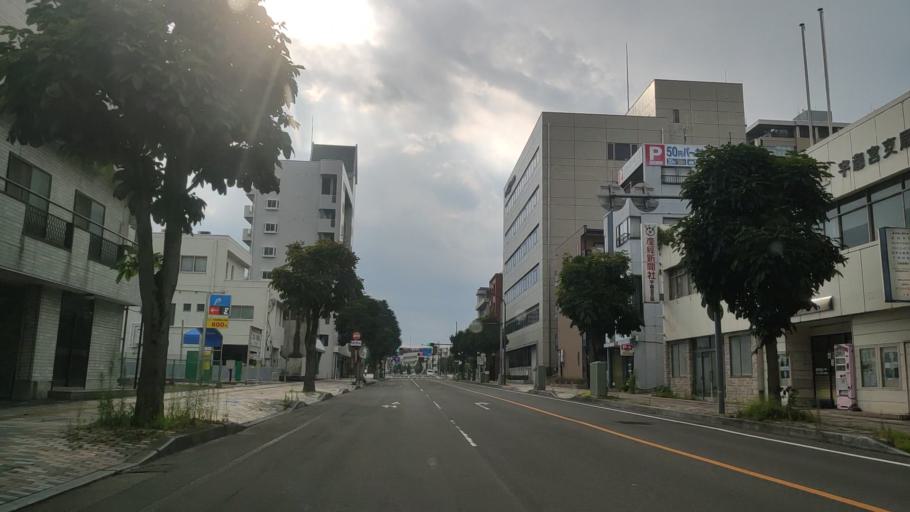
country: JP
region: Tochigi
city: Utsunomiya-shi
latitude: 36.5643
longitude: 139.8858
